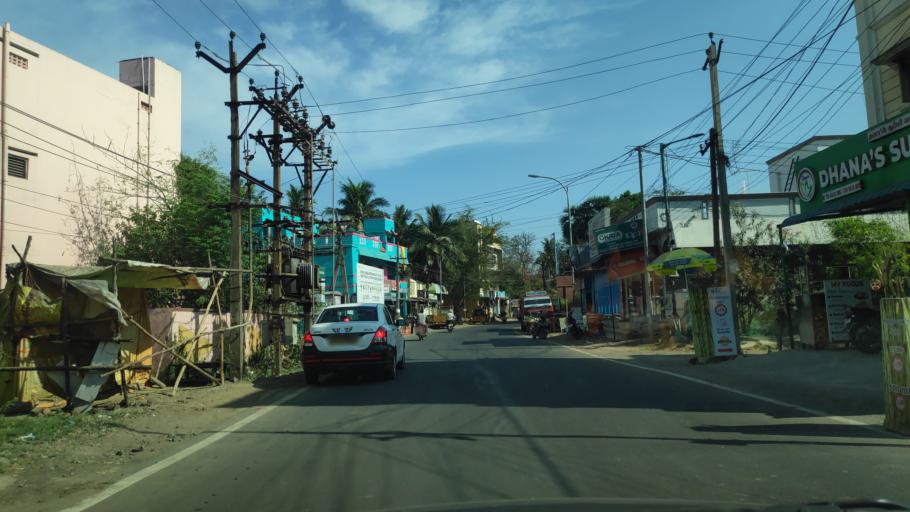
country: IN
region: Tamil Nadu
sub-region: Thiruvallur
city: Ambattur
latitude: 13.1196
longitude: 80.1688
